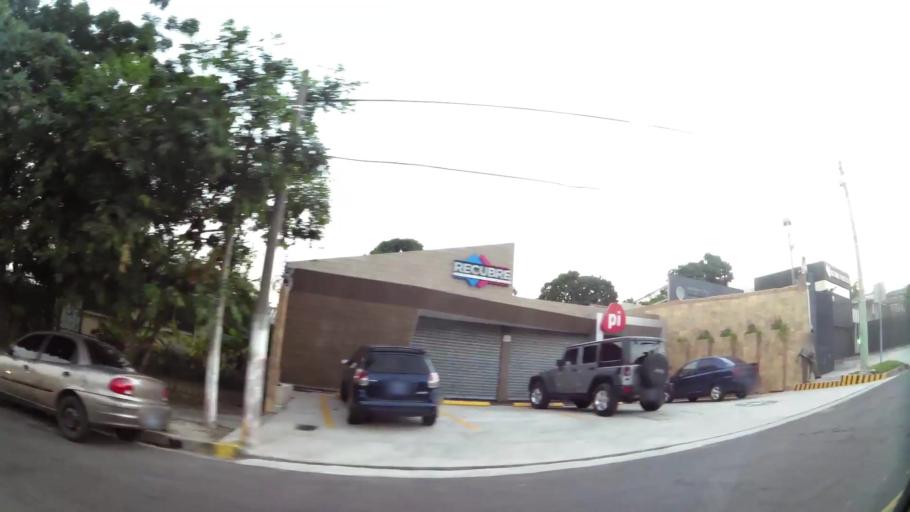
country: SV
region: La Libertad
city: Antiguo Cuscatlan
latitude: 13.6972
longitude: -89.2312
